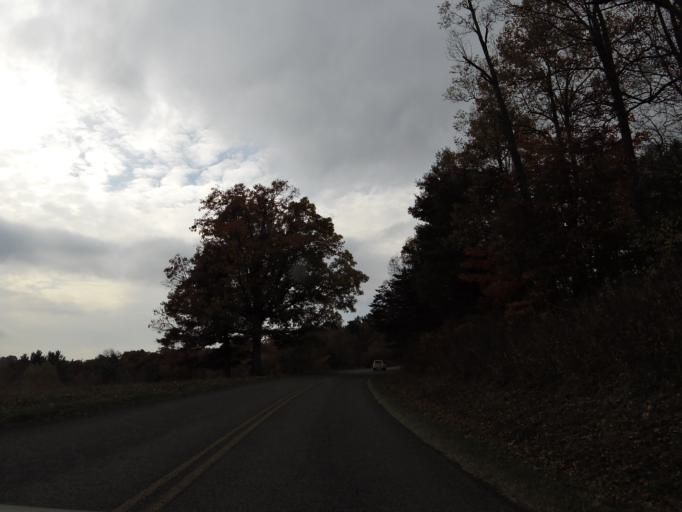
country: US
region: Virginia
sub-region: Carroll County
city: Woodlawn
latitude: 36.6068
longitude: -80.8057
